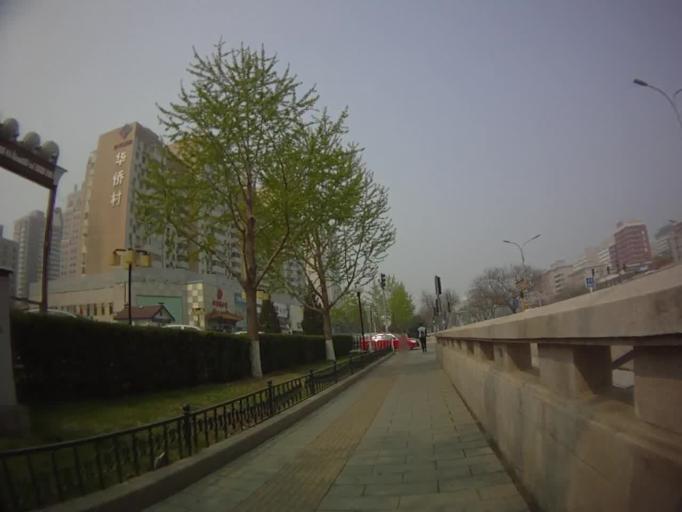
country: CN
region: Beijing
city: Chaowai
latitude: 39.9068
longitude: 116.4359
